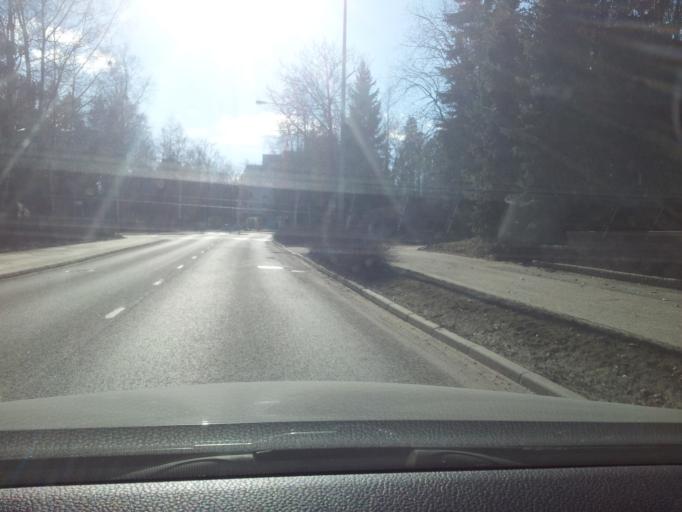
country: FI
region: Uusimaa
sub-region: Helsinki
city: Koukkuniemi
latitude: 60.1613
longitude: 24.7906
